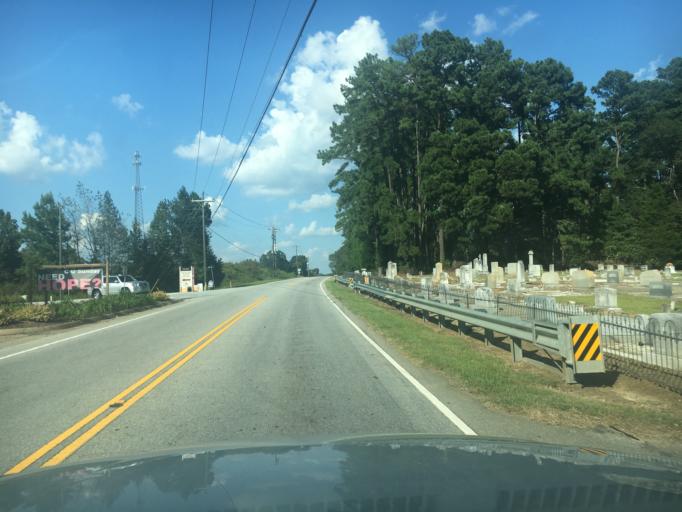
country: US
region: South Carolina
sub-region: Greenville County
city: Simpsonville
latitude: 34.6782
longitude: -82.2570
